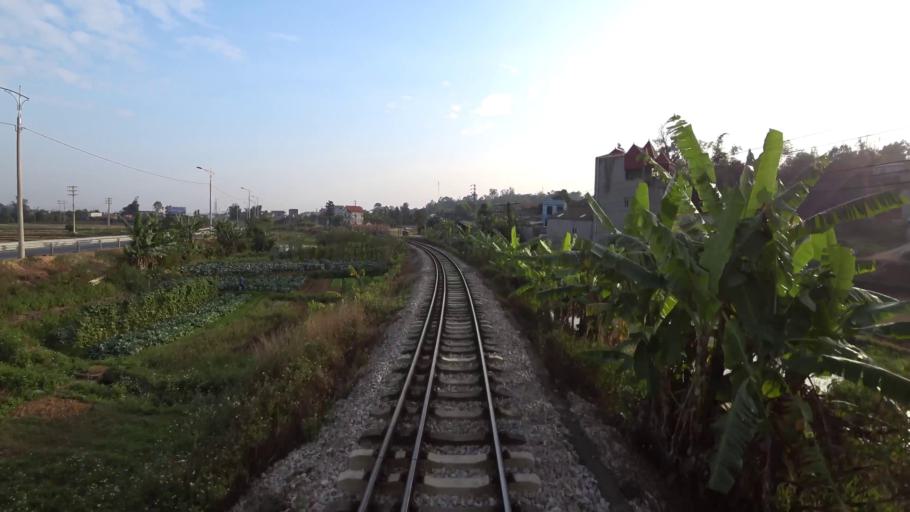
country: VN
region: Lang Son
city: Thi Tran Cao Loc
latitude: 21.8895
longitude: 106.7452
